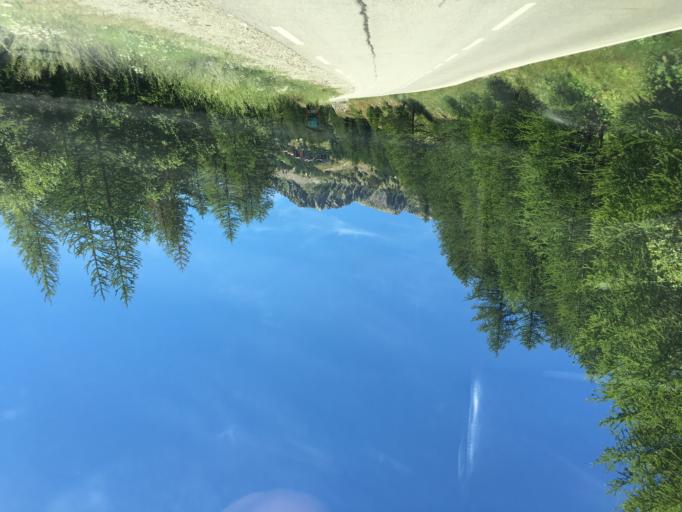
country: IT
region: Piedmont
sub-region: Provincia di Cuneo
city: Vinadio
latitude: 44.1921
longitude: 7.1410
